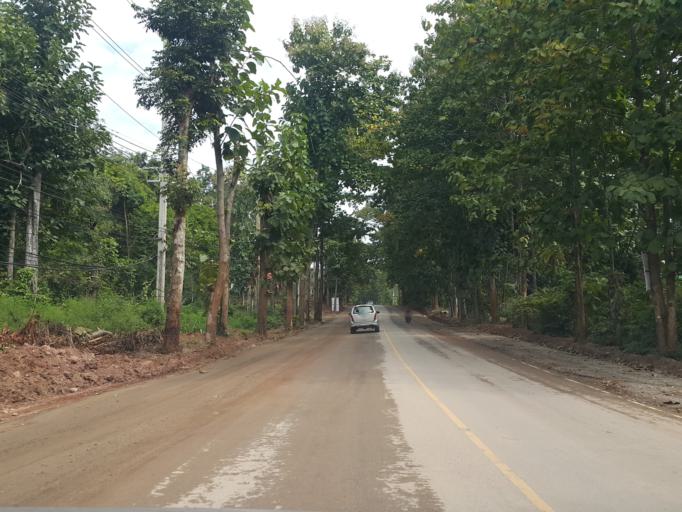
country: TH
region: Mae Hong Son
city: Mae Hong Son
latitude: 19.3316
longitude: 97.9649
